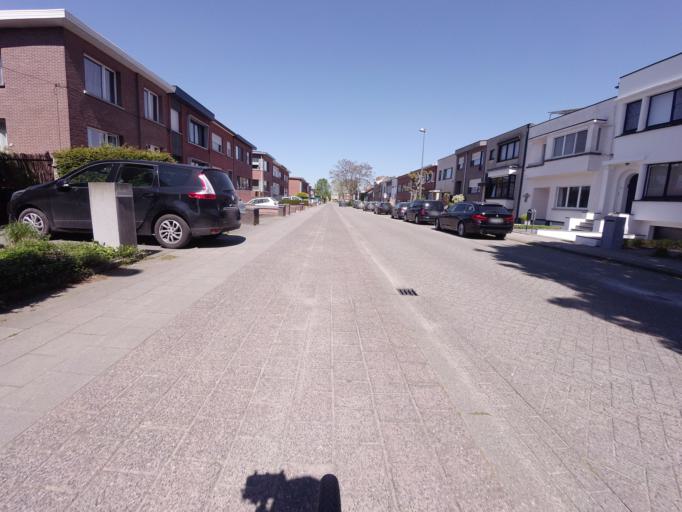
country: BE
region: Flanders
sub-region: Provincie Antwerpen
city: Hove
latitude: 51.1666
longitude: 4.4711
